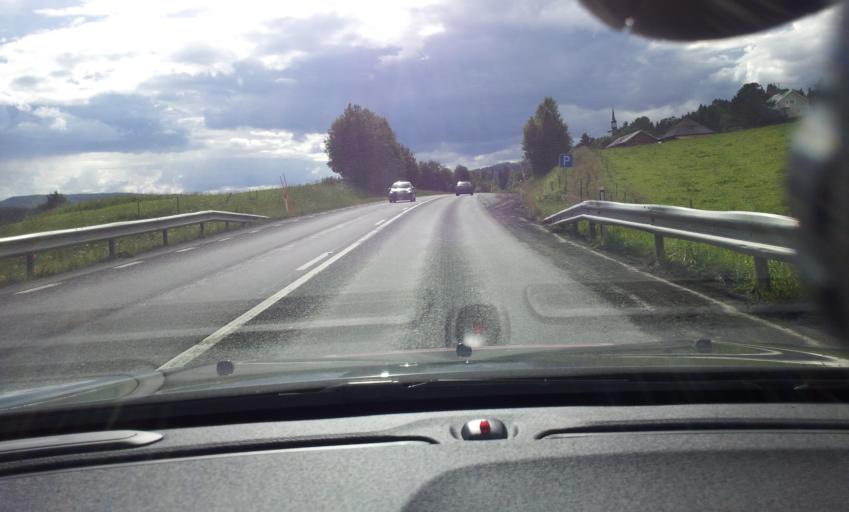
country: SE
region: Jaemtland
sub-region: Are Kommun
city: Jarpen
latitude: 63.3287
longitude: 13.3978
